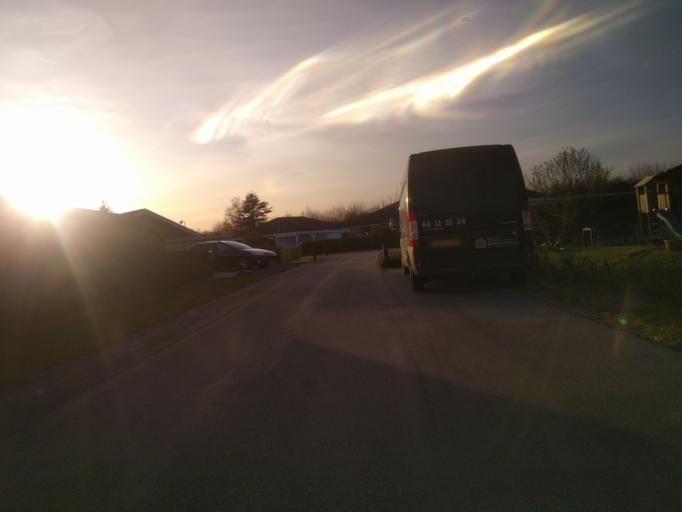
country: DK
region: South Denmark
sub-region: Odense Kommune
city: Bullerup
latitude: 55.4335
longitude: 10.4874
